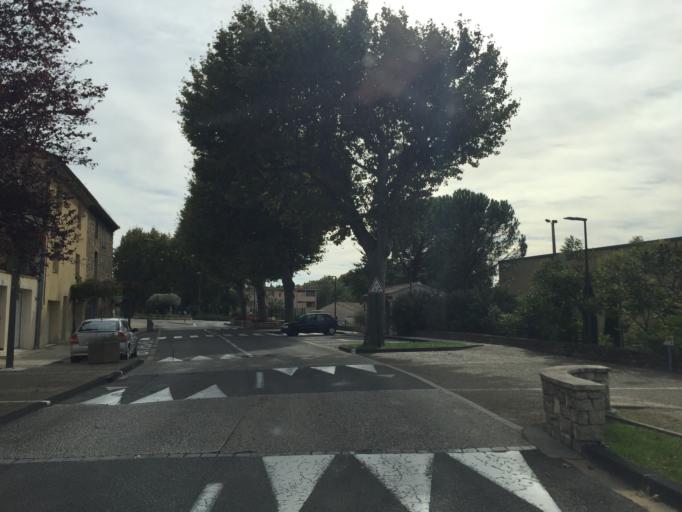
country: FR
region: Provence-Alpes-Cote d'Azur
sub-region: Departement du Vaucluse
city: Mondragon
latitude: 44.2351
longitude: 4.7128
